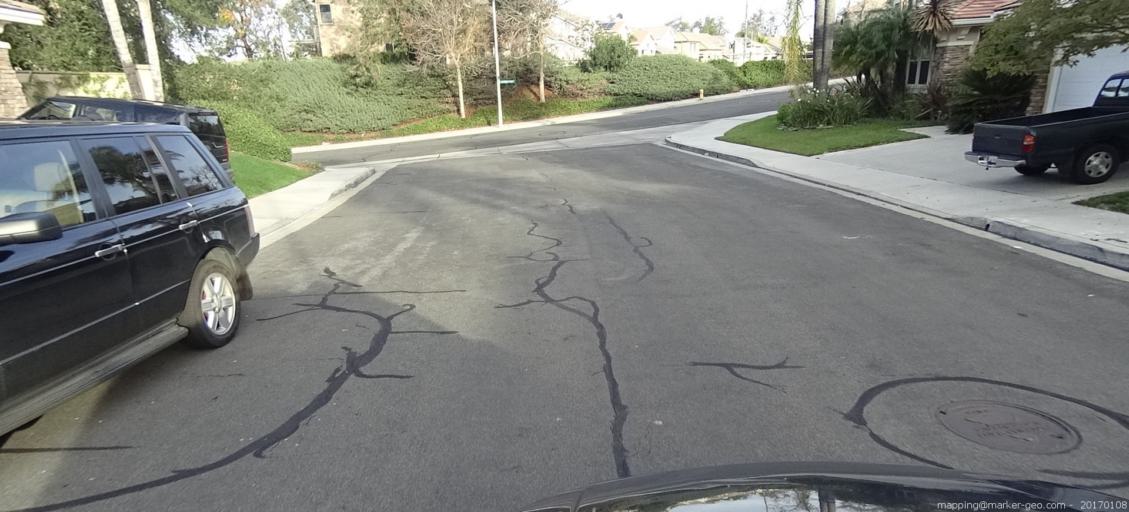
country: US
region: California
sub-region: Orange County
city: Las Flores
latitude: 33.5879
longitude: -117.6236
